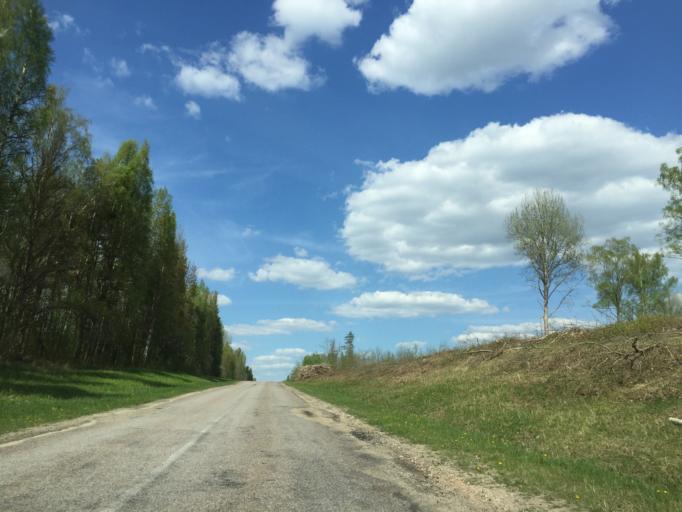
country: LV
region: Limbazu Rajons
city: Limbazi
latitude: 57.4092
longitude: 24.6933
